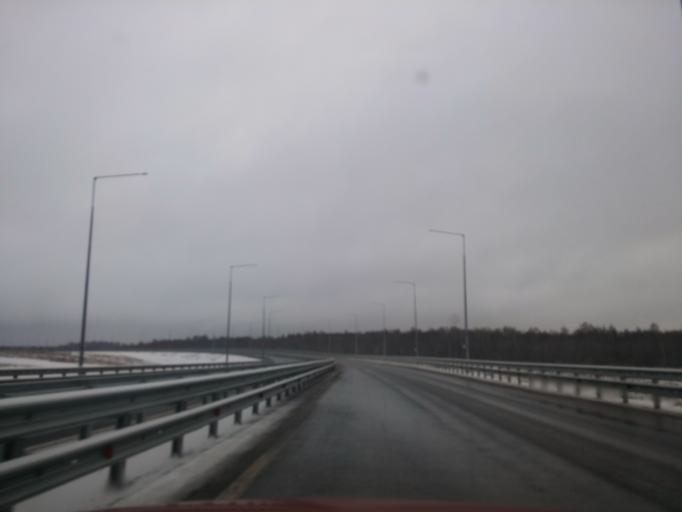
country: RU
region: Tverskaya
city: Likhoslavl'
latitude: 56.9601
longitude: 35.4819
